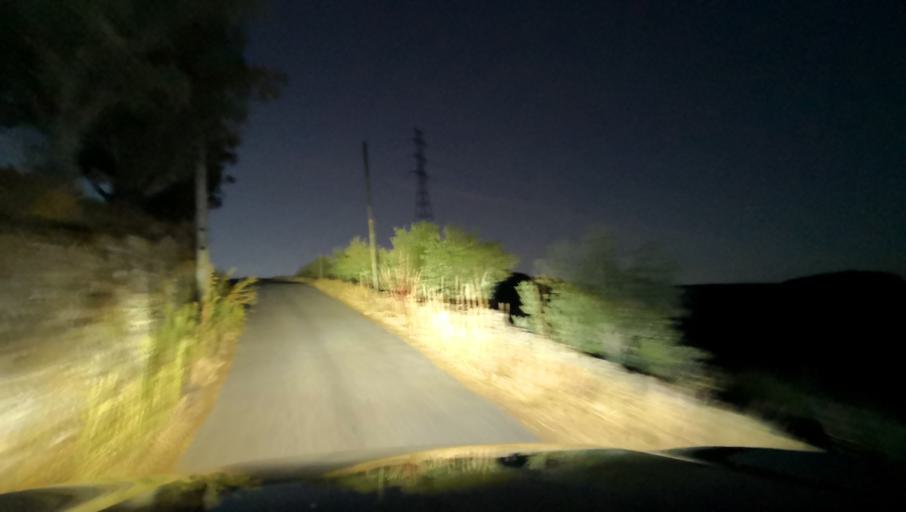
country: PT
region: Viseu
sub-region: Armamar
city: Armamar
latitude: 41.1624
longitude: -7.6977
